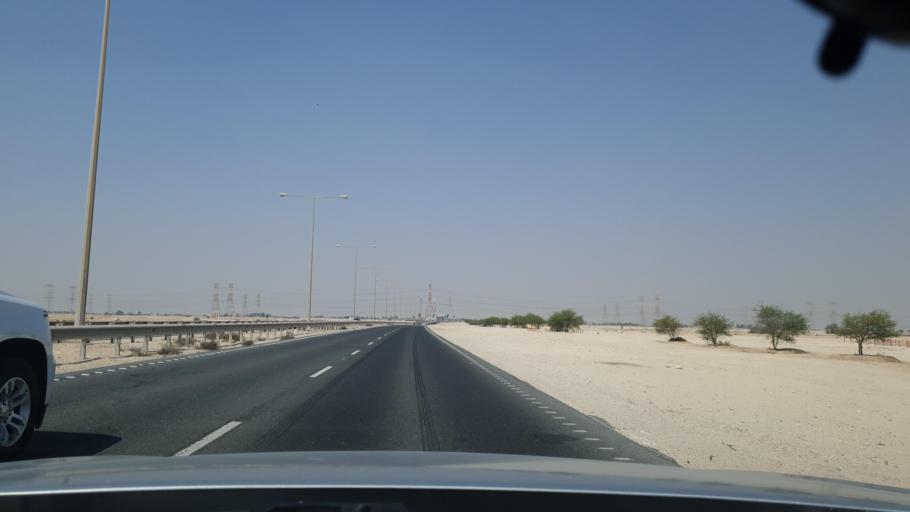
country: QA
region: Al Khawr
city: Al Khawr
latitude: 25.7473
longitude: 51.4805
